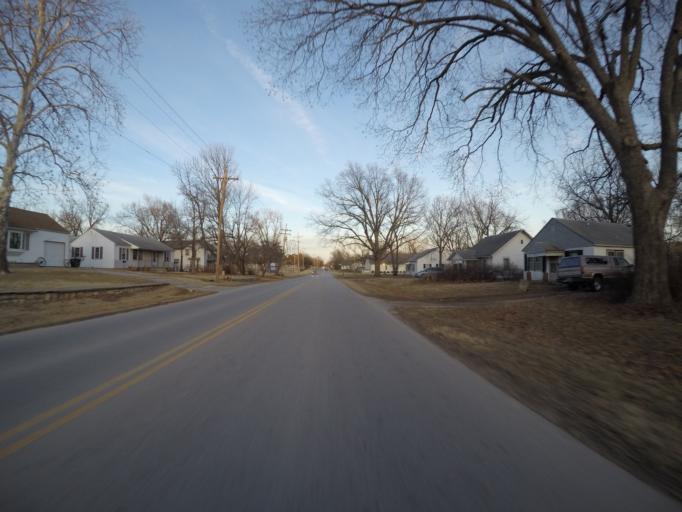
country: US
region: Kansas
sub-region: Morris County
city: Council Grove
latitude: 38.6569
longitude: -96.5050
